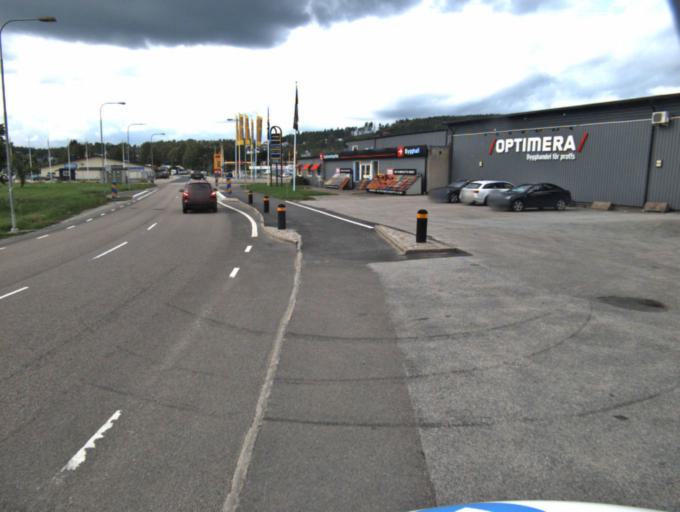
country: SE
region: Vaestra Goetaland
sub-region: Ulricehamns Kommun
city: Ulricehamn
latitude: 57.8038
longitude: 13.4117
